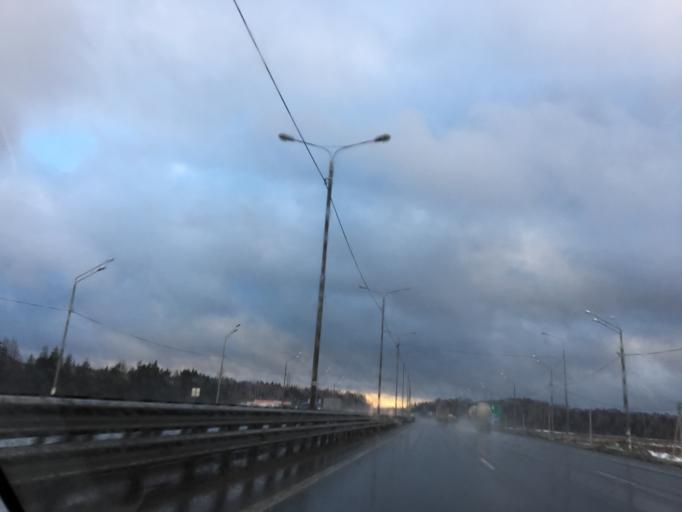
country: RU
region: Moskovskaya
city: Novyy Byt
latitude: 55.0494
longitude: 37.5599
